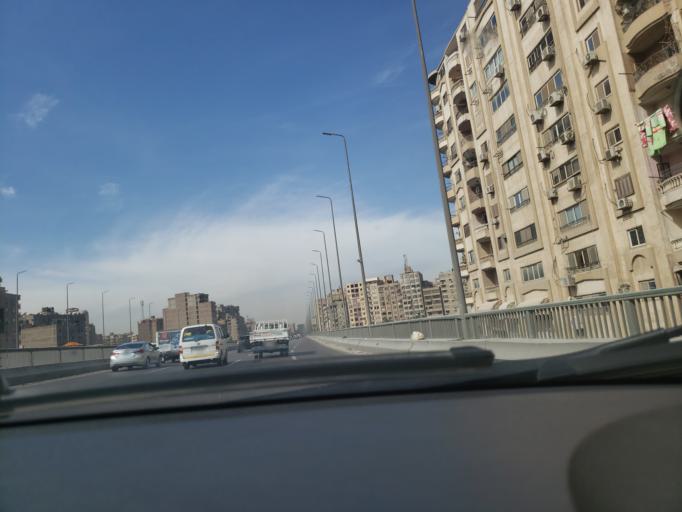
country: EG
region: Al Jizah
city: Al Jizah
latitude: 29.9798
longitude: 31.1594
